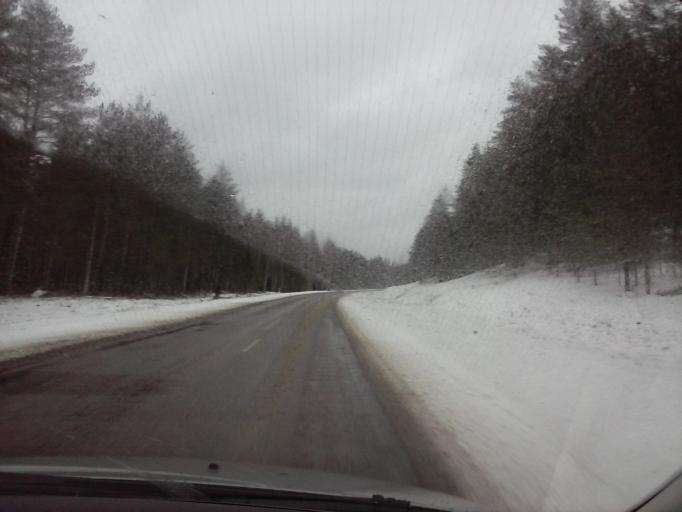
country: LV
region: Strenci
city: Seda
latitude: 57.6659
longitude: 25.8751
